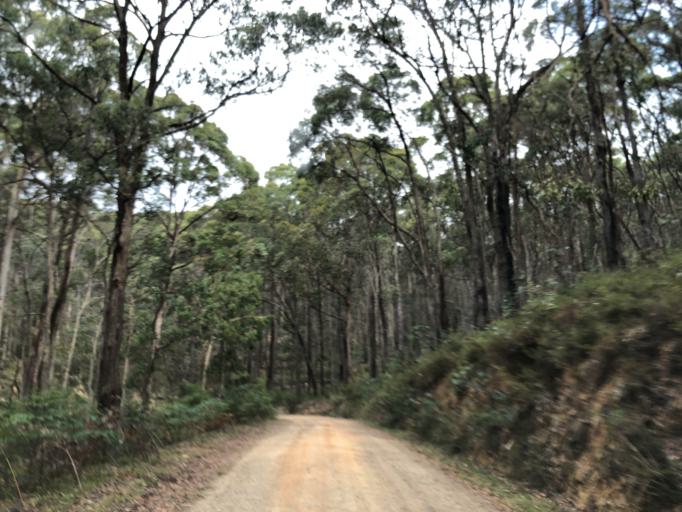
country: AU
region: Victoria
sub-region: Moorabool
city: Bacchus Marsh
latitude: -37.4595
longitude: 144.2713
